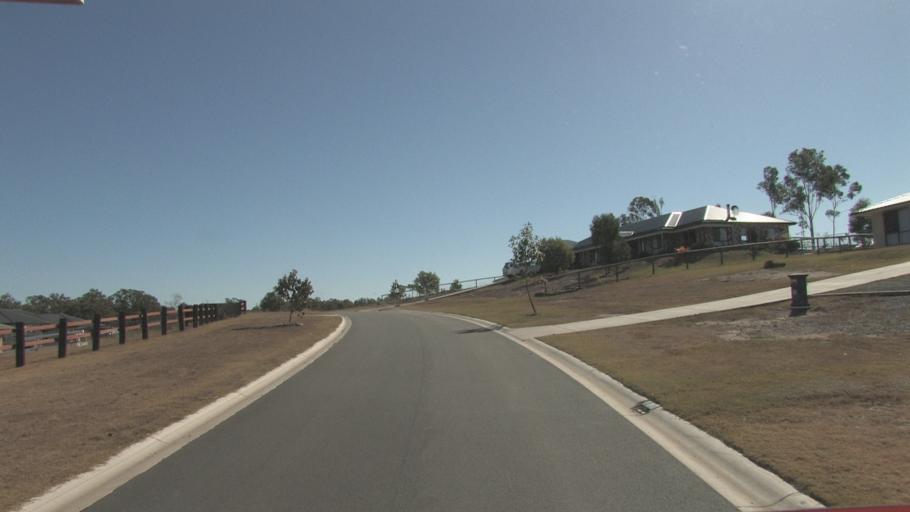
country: AU
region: Queensland
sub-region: Logan
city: Cedar Vale
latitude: -27.8638
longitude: 153.0436
